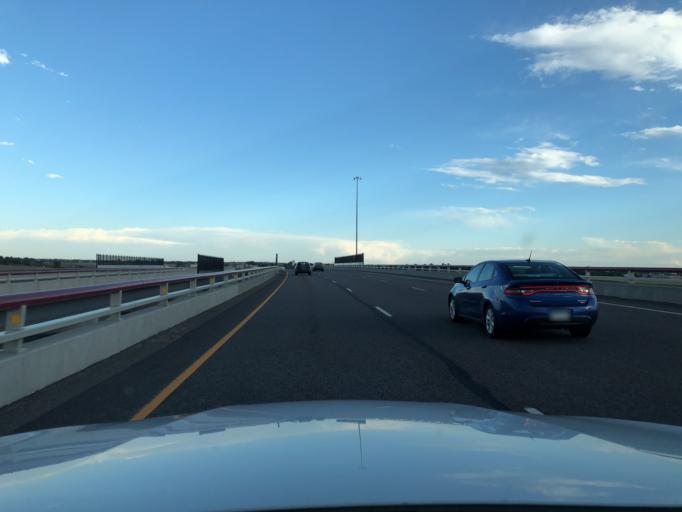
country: US
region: Colorado
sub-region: Adams County
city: Todd Creek
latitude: 39.9346
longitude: -104.8464
